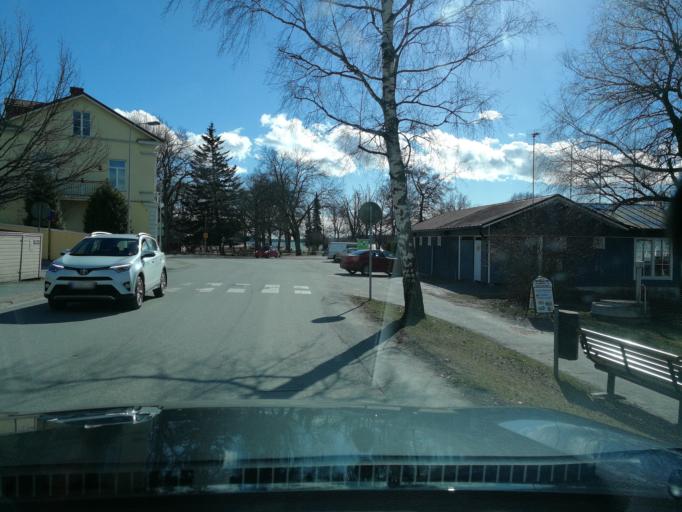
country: FI
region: Uusimaa
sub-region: Raaseporin
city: Ekenaes
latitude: 59.9771
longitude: 23.4332
